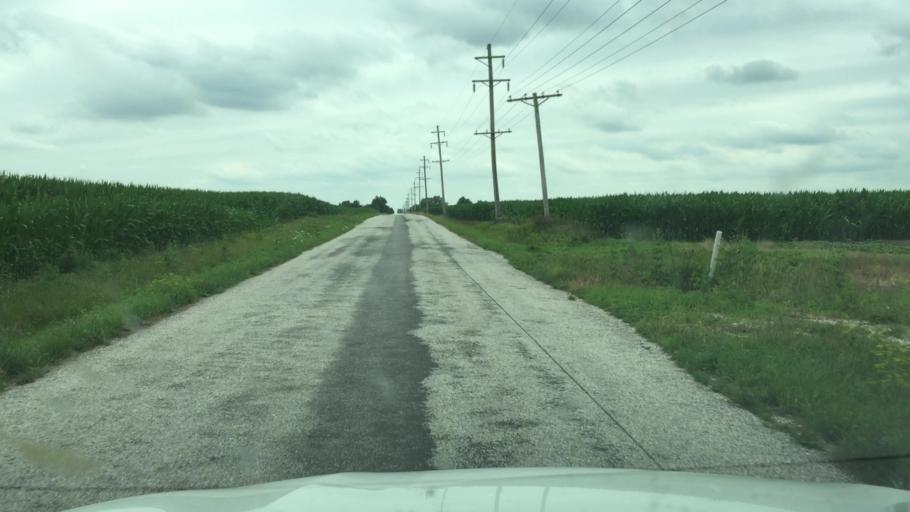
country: US
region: Illinois
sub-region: Hancock County
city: Carthage
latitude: 40.3381
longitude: -91.0824
